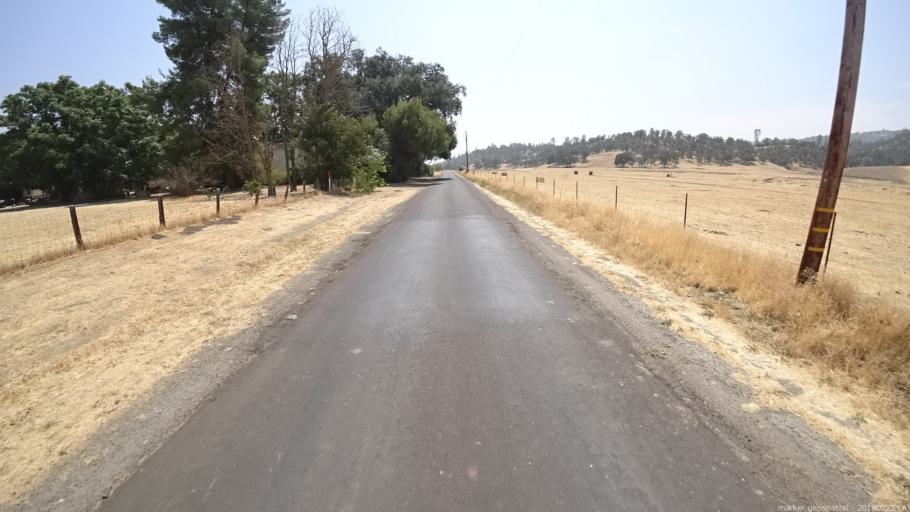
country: US
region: California
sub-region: Fresno County
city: Coalinga
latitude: 35.9498
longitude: -120.4732
